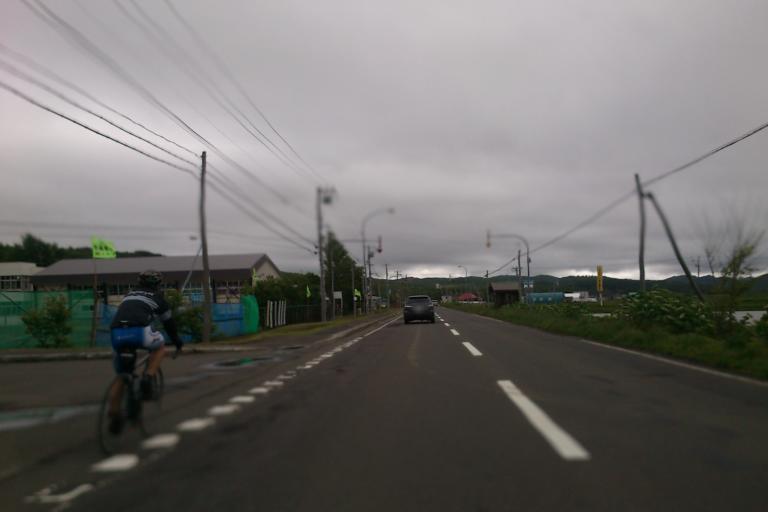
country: JP
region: Hokkaido
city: Ishikari
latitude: 43.3176
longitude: 141.4265
